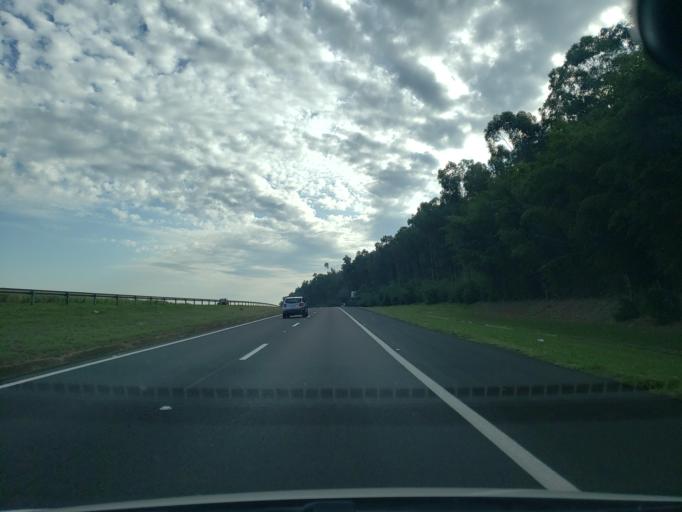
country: BR
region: Sao Paulo
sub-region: Guararapes
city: Guararapes
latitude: -21.1998
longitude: -50.5653
